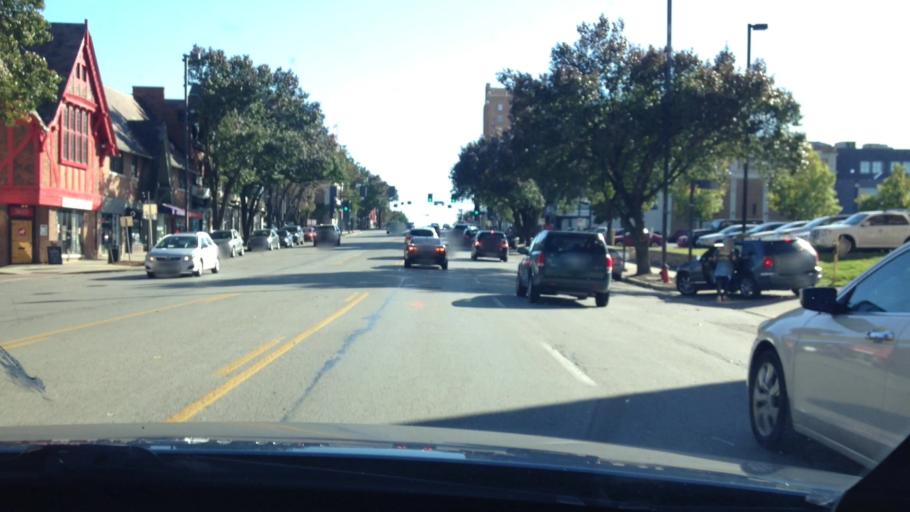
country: US
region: Kansas
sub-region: Johnson County
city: Westwood
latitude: 39.0625
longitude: -94.5905
